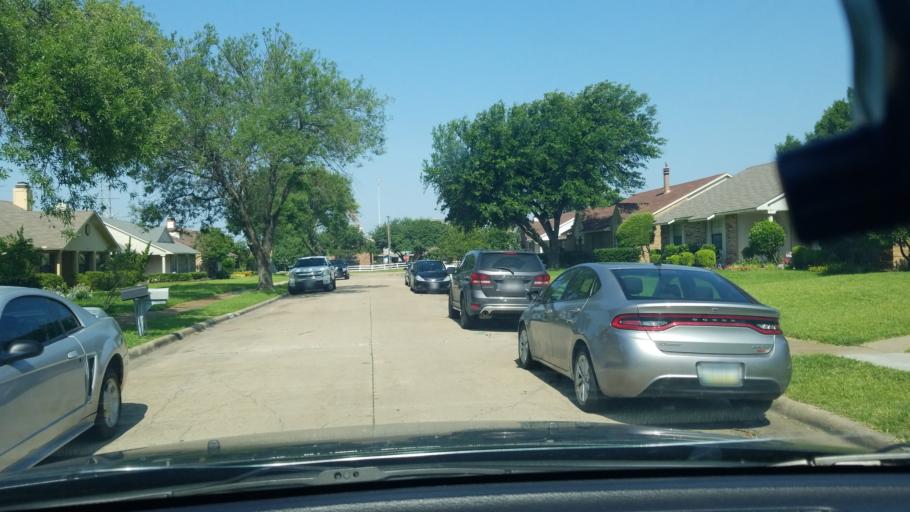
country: US
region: Texas
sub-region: Dallas County
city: Mesquite
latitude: 32.8203
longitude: -96.6257
